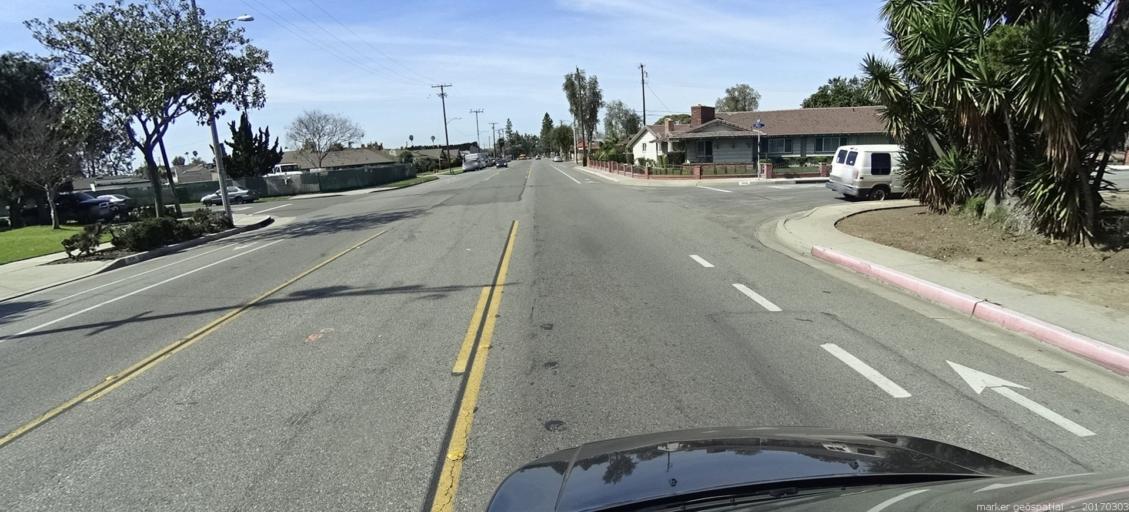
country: US
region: California
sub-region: Orange County
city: Garden Grove
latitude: 33.7959
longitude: -117.9384
